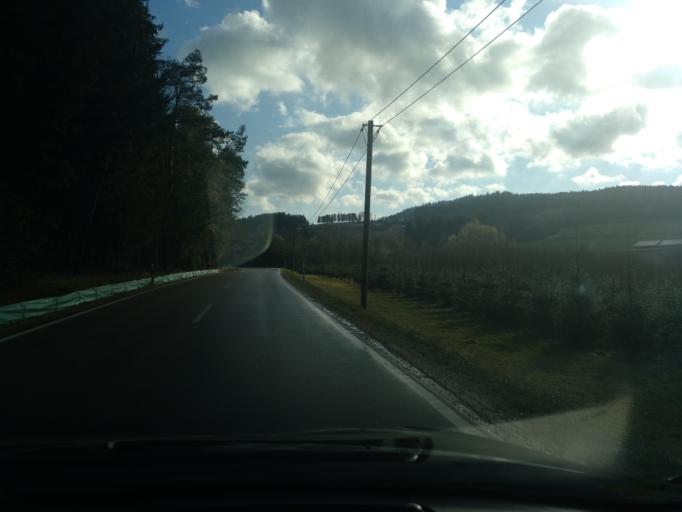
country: DE
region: Bavaria
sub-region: Lower Bavaria
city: Konzell
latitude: 49.1124
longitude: 12.7147
